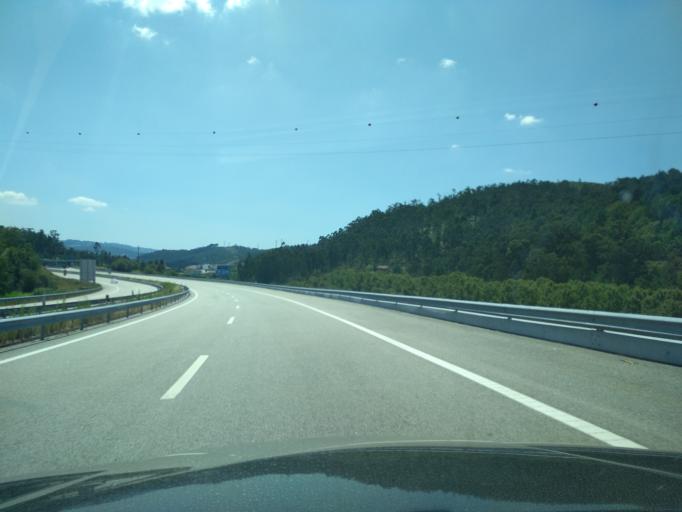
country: PT
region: Braga
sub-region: Fafe
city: Fafe
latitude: 41.4340
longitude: -8.1786
